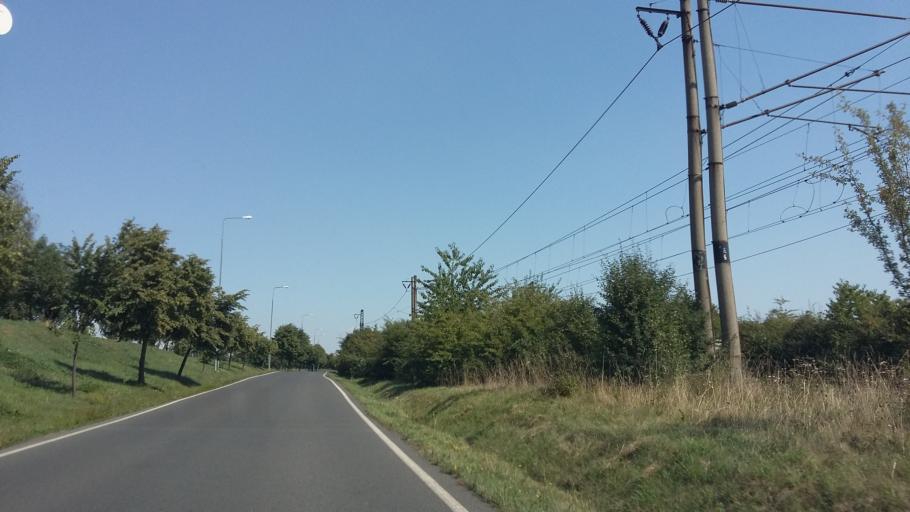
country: CZ
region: Central Bohemia
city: Zelenec
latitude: 50.1251
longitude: 14.6425
